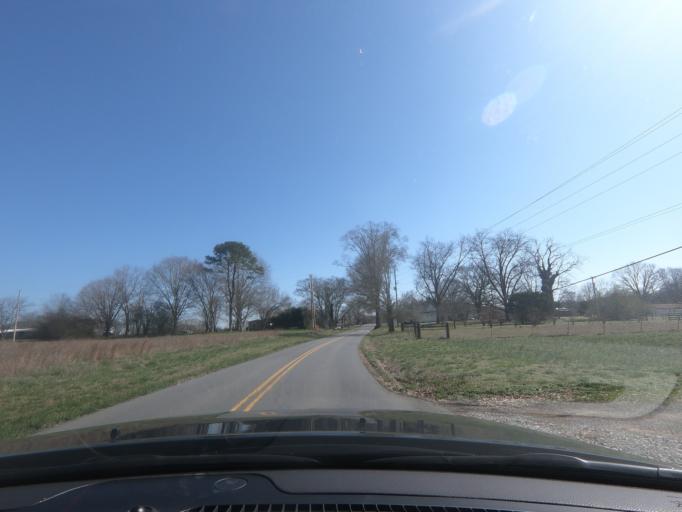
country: US
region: Georgia
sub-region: Gordon County
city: Calhoun
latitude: 34.4613
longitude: -85.0146
